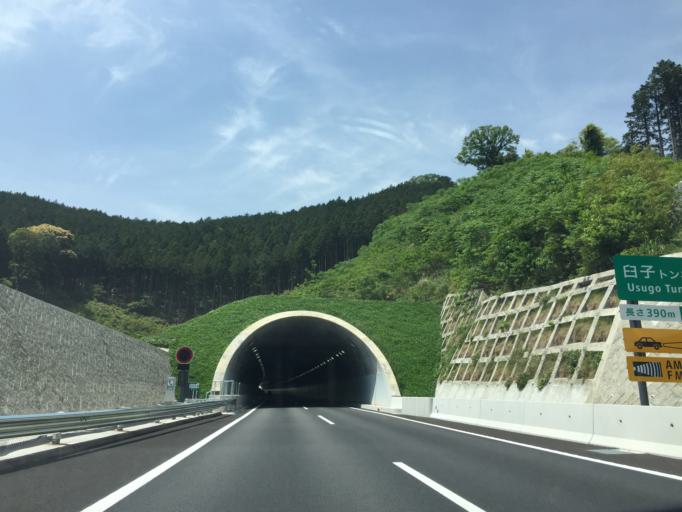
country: JP
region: Aichi
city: Shinshiro
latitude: 34.9104
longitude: 137.4601
